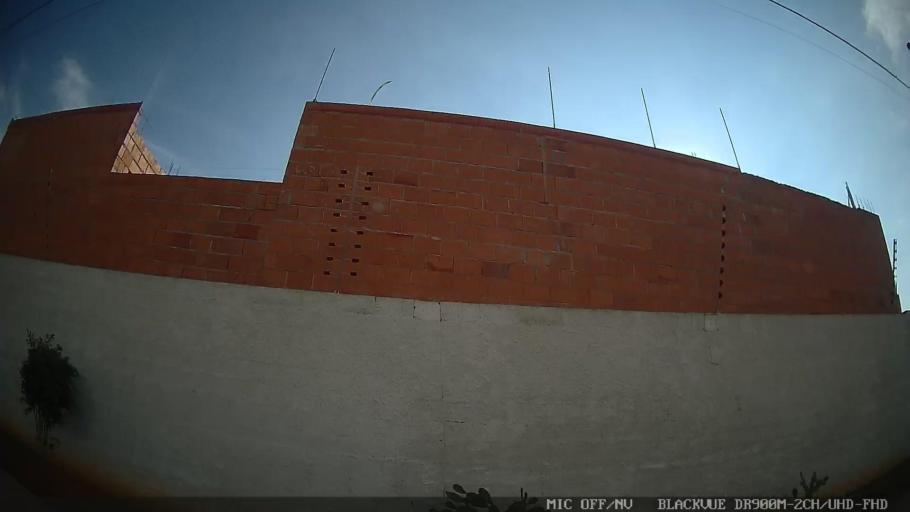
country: BR
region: Sao Paulo
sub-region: Indaiatuba
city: Indaiatuba
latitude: -23.0893
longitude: -47.2334
